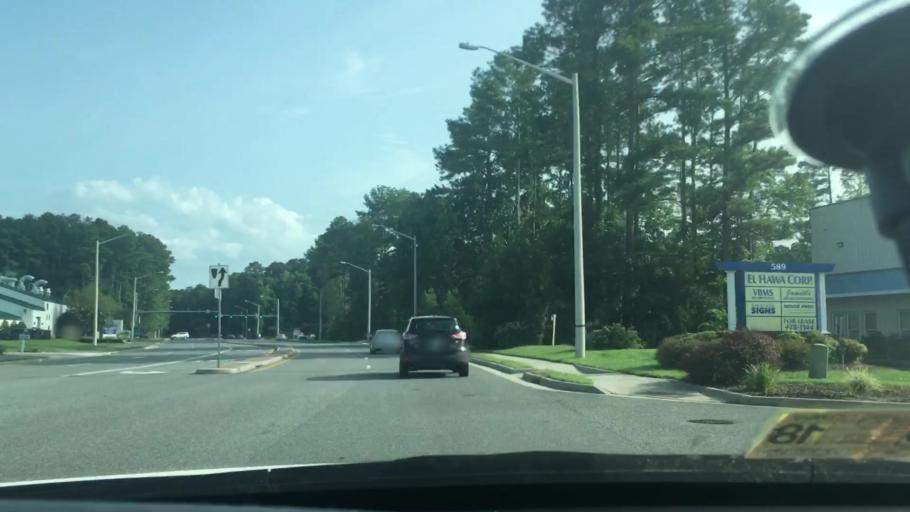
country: US
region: Virginia
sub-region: City of Virginia Beach
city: Virginia Beach
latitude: 36.8221
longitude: -76.0002
